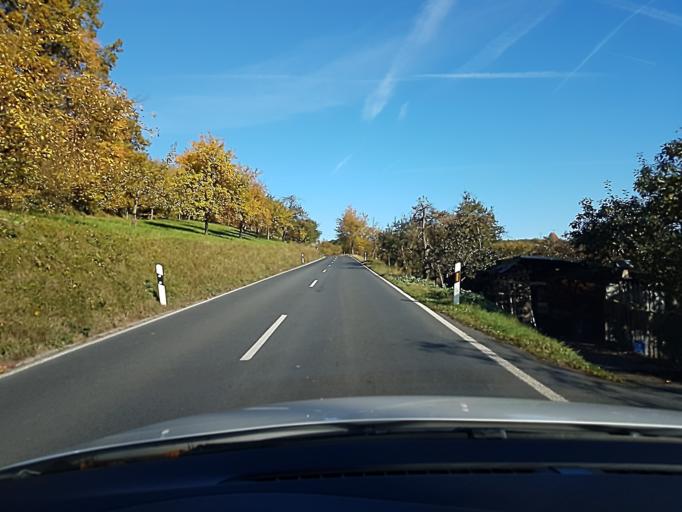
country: DE
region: Bavaria
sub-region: Regierungsbezirk Unterfranken
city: Hausen
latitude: 49.8719
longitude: 9.2213
